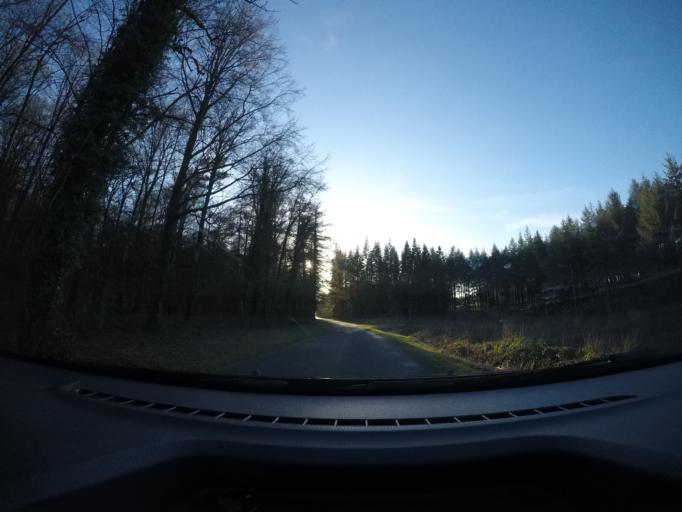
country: BE
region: Wallonia
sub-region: Province du Luxembourg
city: Tintigny
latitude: 49.6796
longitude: 5.4943
